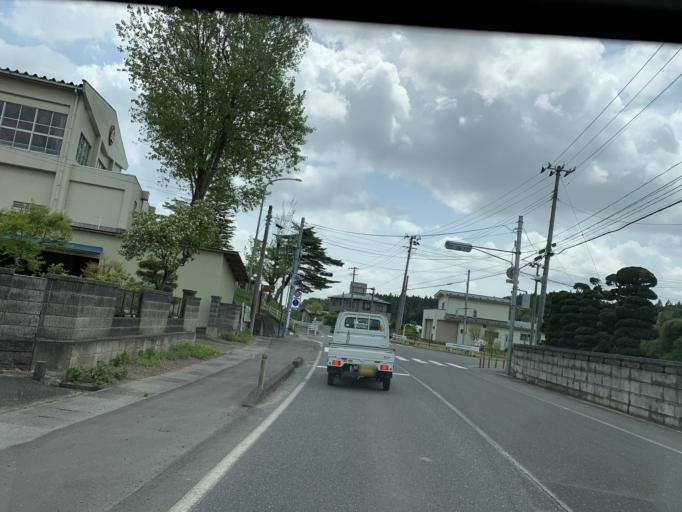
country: JP
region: Miyagi
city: Furukawa
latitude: 38.6930
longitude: 140.9315
